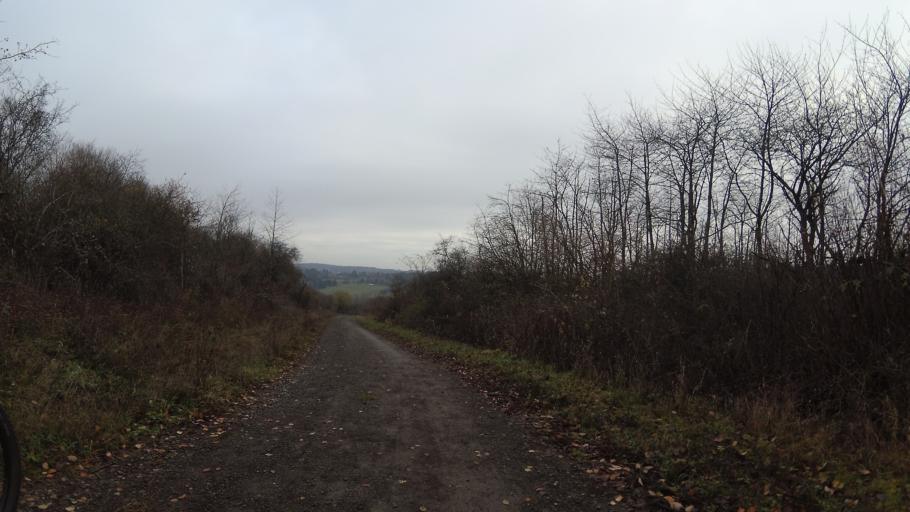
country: DE
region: Saarland
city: Merchweiler
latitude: 49.3540
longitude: 7.0341
